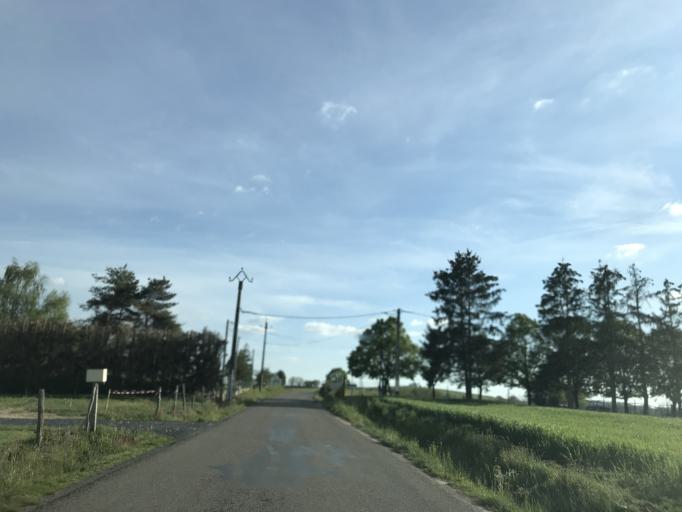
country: FR
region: Auvergne
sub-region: Departement du Puy-de-Dome
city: Courpiere
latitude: 45.7187
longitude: 3.4672
